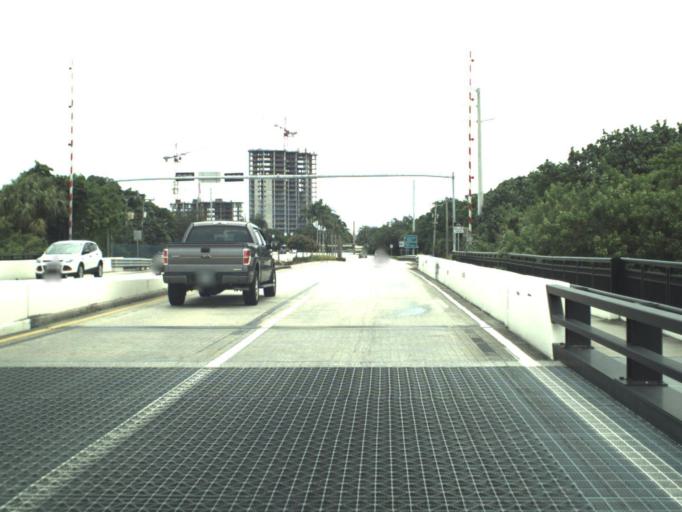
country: US
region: Florida
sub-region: Palm Beach County
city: North Palm Beach
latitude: 26.8316
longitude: -80.0601
